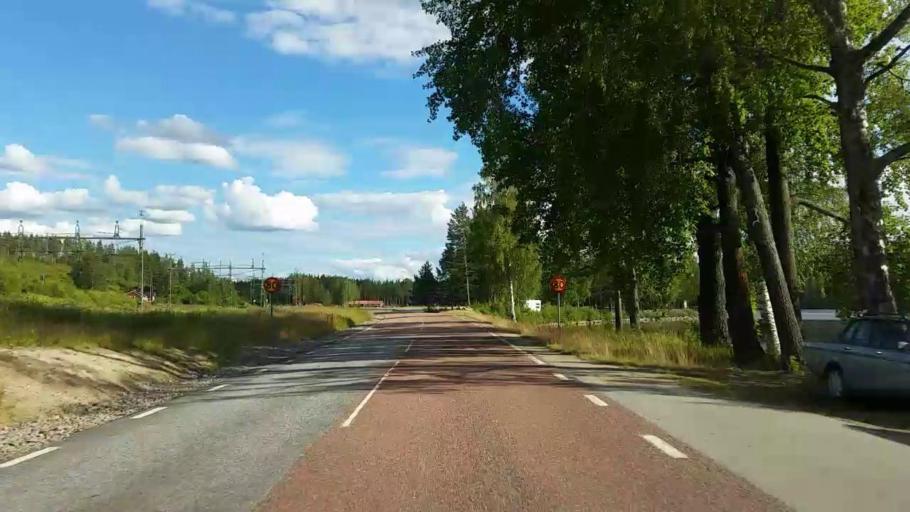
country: SE
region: Gaevleborg
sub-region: Ljusdals Kommun
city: Farila
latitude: 62.0216
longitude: 15.9018
